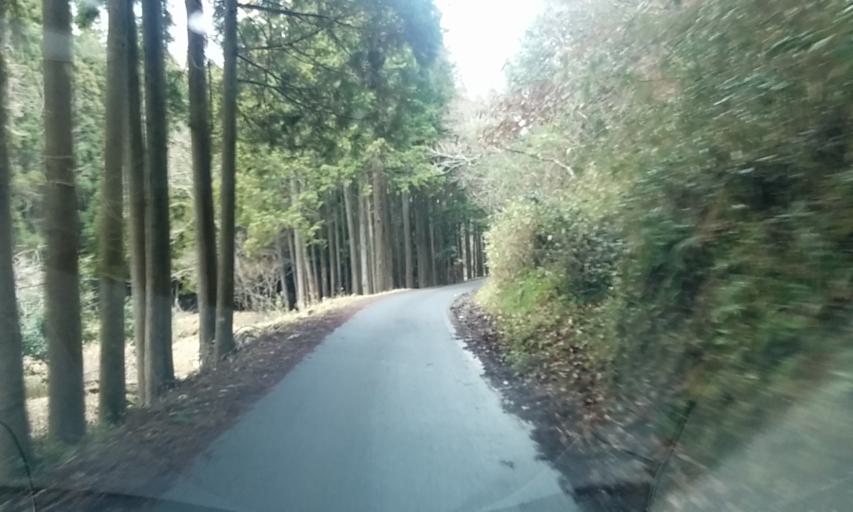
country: JP
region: Kyoto
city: Kameoka
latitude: 35.1113
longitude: 135.4350
